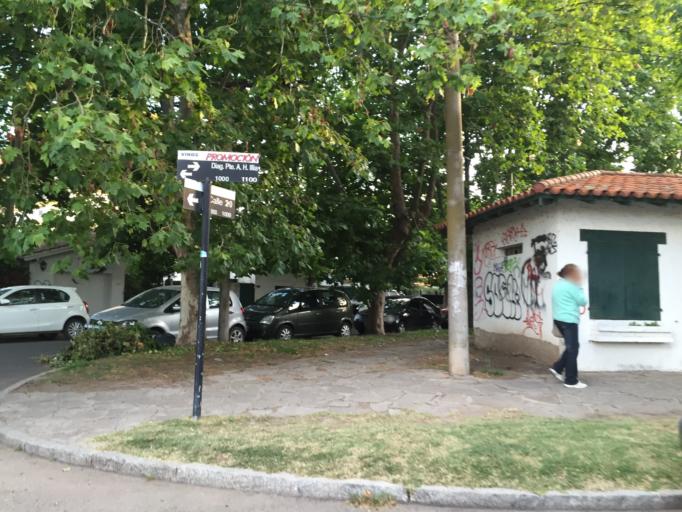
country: AR
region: Buenos Aires
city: Miramar
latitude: -38.2704
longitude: -57.8348
